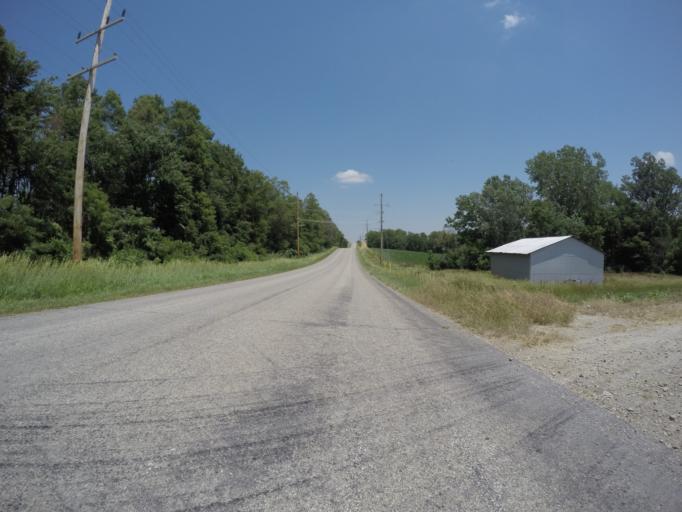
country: US
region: Kansas
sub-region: Doniphan County
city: Troy
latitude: 39.7604
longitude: -95.1387
